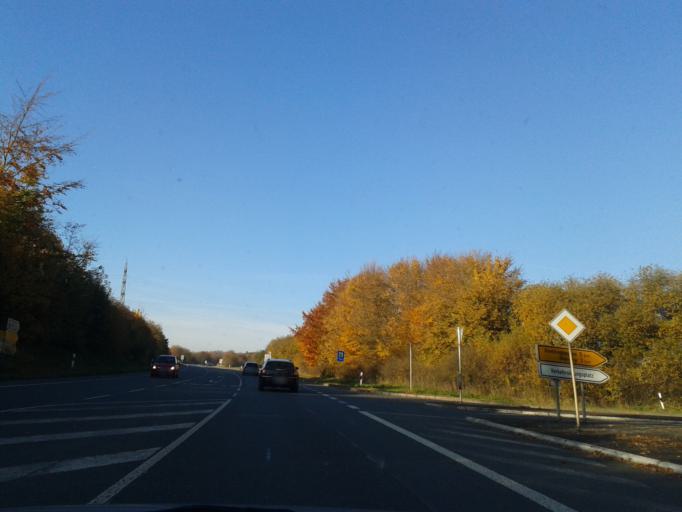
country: DE
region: North Rhine-Westphalia
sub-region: Regierungsbezirk Arnsberg
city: Ruthen
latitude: 51.5075
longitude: 8.4546
